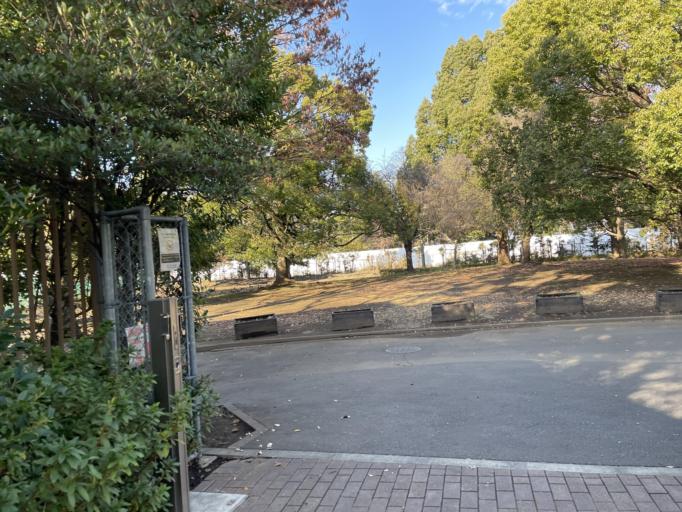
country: JP
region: Saitama
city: Asaka
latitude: 35.7796
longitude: 139.5859
